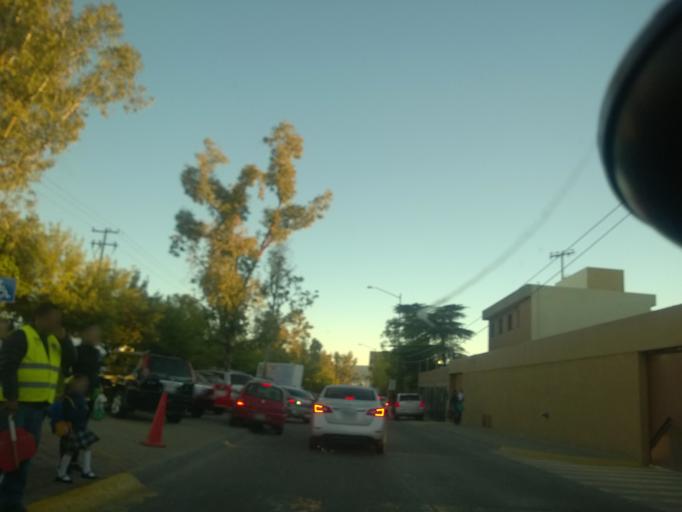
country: MX
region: Guanajuato
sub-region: Leon
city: La Ermita
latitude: 21.1521
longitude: -101.7028
